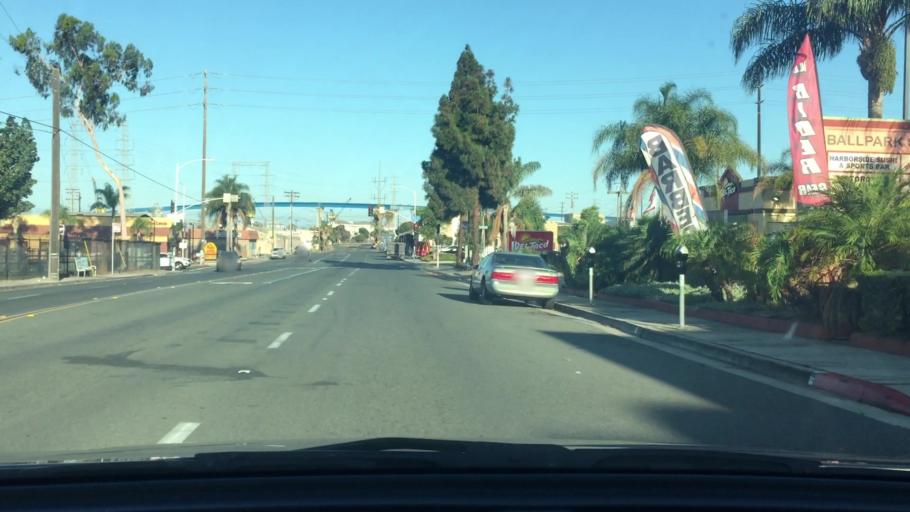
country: US
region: California
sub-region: San Diego County
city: San Diego
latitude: 32.6929
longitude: -117.1328
